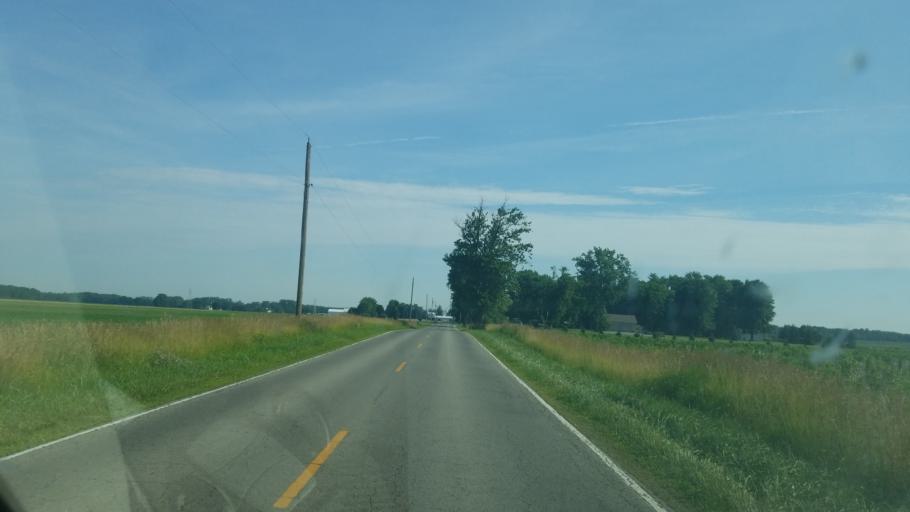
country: US
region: Ohio
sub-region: Hancock County
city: Findlay
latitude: 41.0175
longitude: -83.5881
